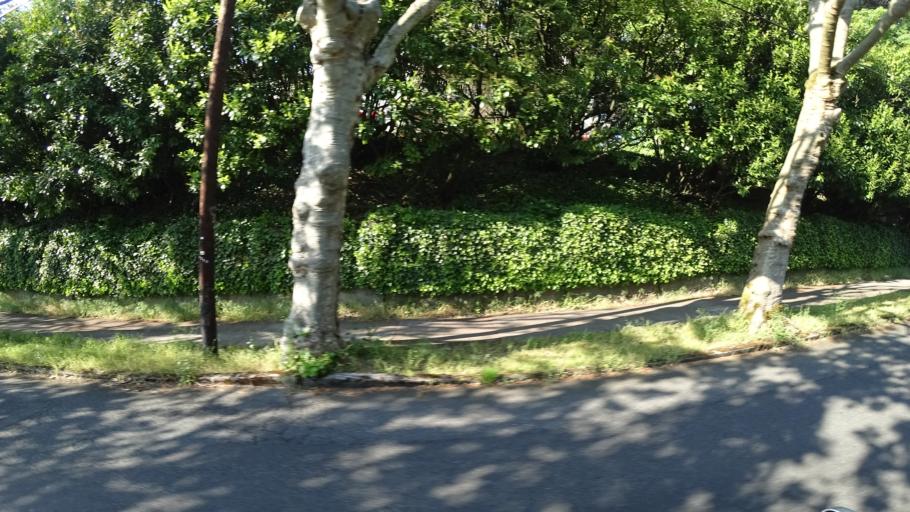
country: US
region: Oregon
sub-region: Multnomah County
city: Portland
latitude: 45.5497
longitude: -122.6376
